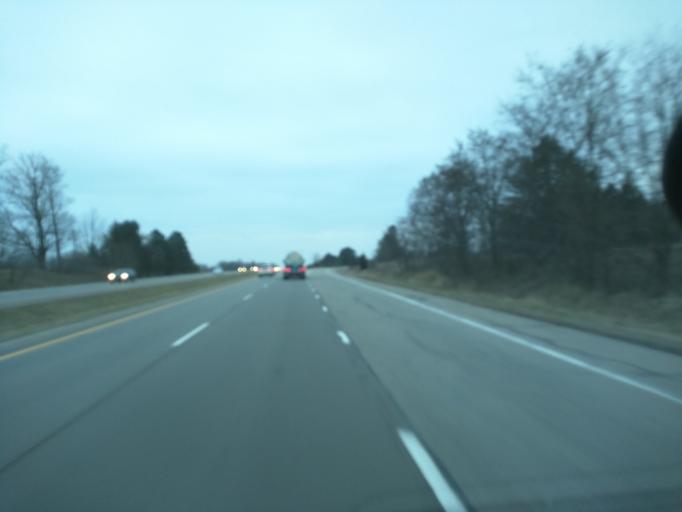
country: US
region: Michigan
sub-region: Ingham County
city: Leslie
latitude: 42.3844
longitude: -84.4292
